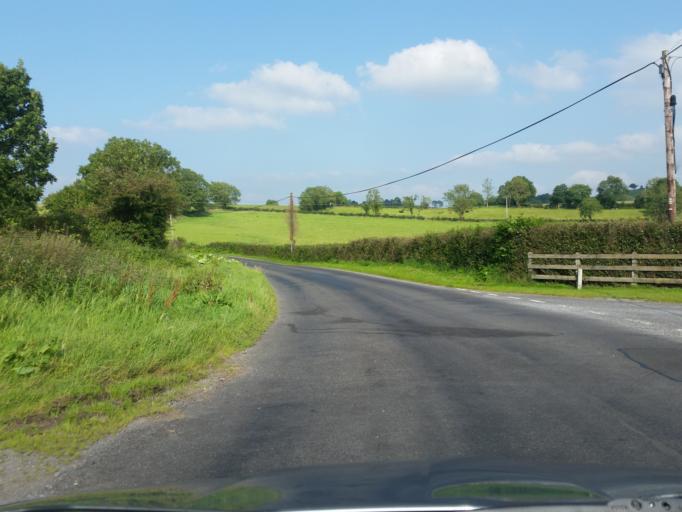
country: GB
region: Northern Ireland
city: Ballinamallard
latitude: 54.3658
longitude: -7.6018
